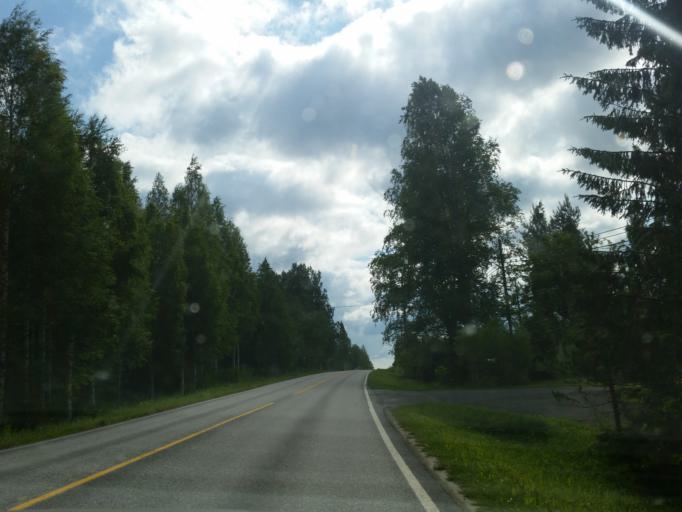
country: FI
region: Northern Savo
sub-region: Kuopio
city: Kuopio
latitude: 62.8471
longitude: 27.3946
